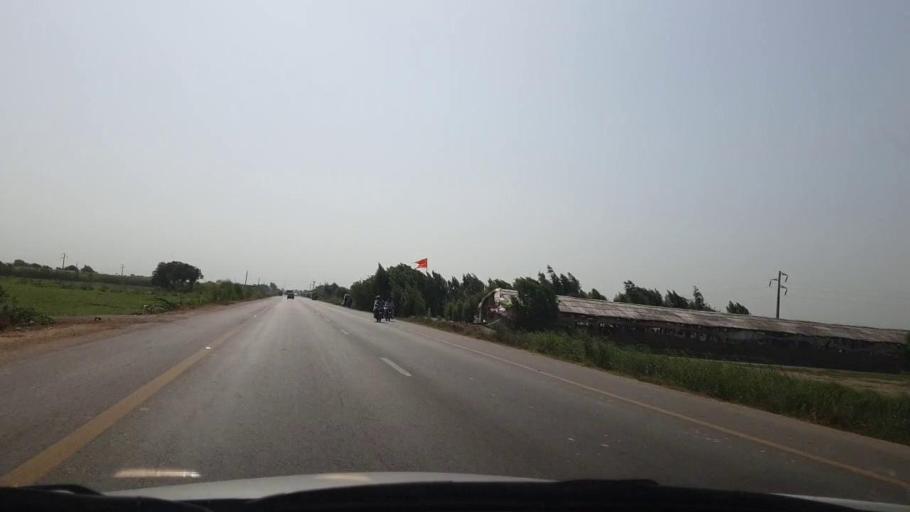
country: PK
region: Sindh
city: Tando Muhammad Khan
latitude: 25.1162
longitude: 68.5750
